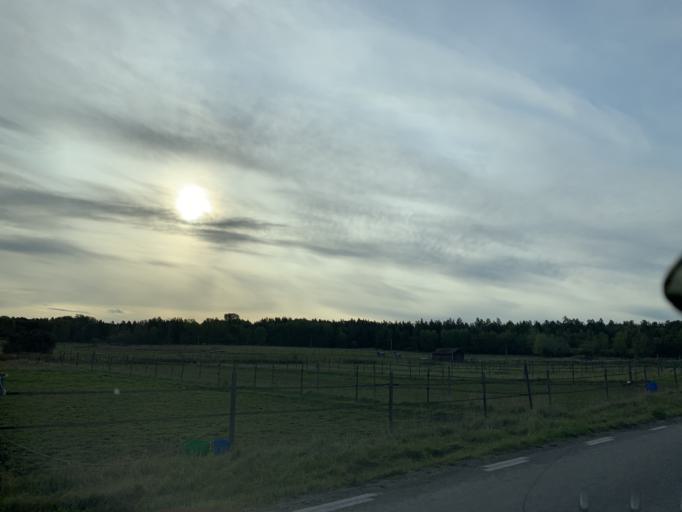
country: SE
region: Stockholm
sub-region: Haninge Kommun
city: Jordbro
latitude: 59.0612
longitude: 18.0670
